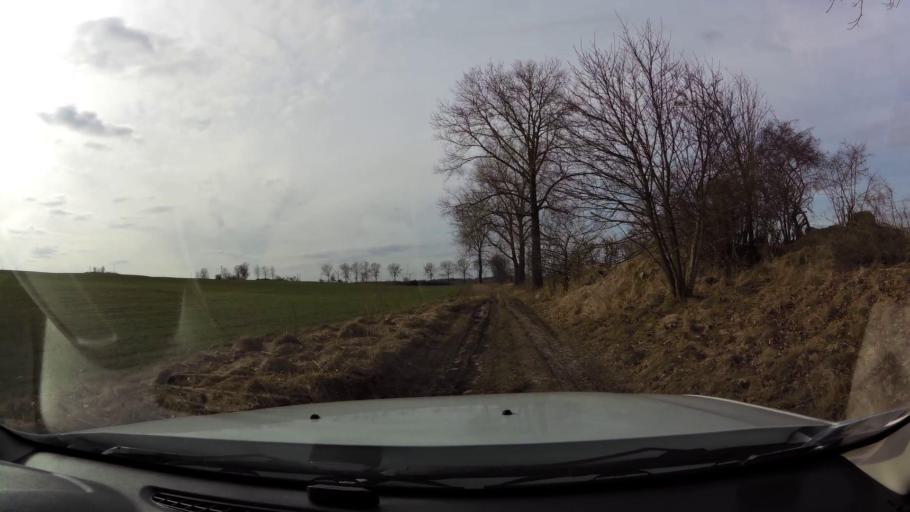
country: PL
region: West Pomeranian Voivodeship
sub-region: Powiat drawski
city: Drawsko Pomorskie
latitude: 53.5235
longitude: 15.7658
